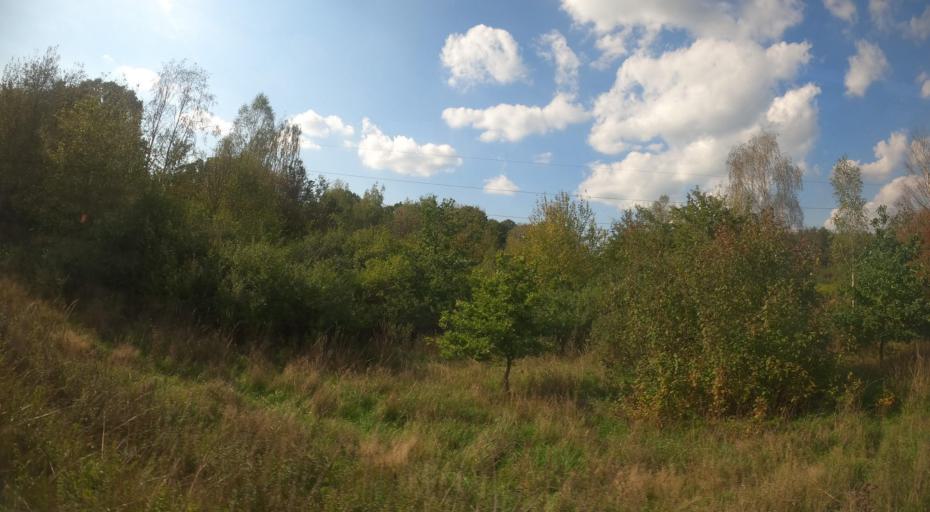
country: PL
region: Lubusz
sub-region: Powiat zielonogorski
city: Swidnica
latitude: 51.9006
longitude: 15.3170
